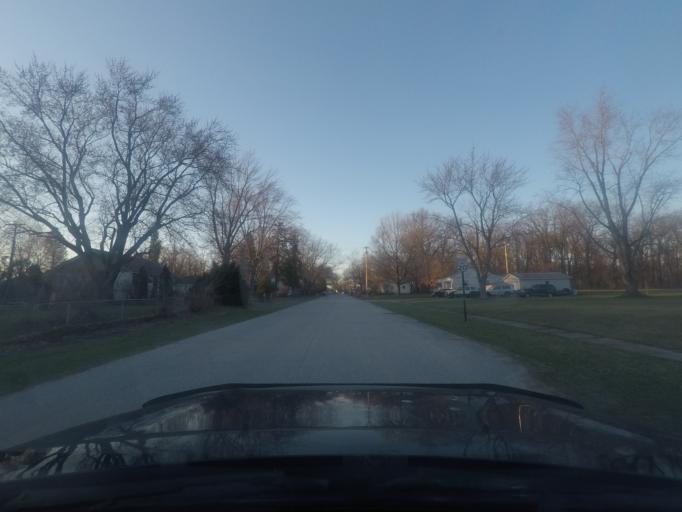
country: US
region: Indiana
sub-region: LaPorte County
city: Kingsford Heights
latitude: 41.4767
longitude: -86.6969
